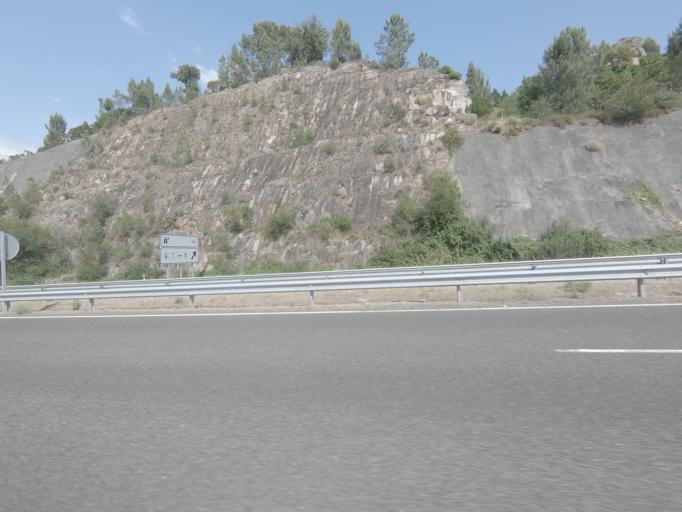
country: ES
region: Galicia
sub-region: Provincia de Ourense
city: Ourense
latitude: 42.2981
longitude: -7.8770
